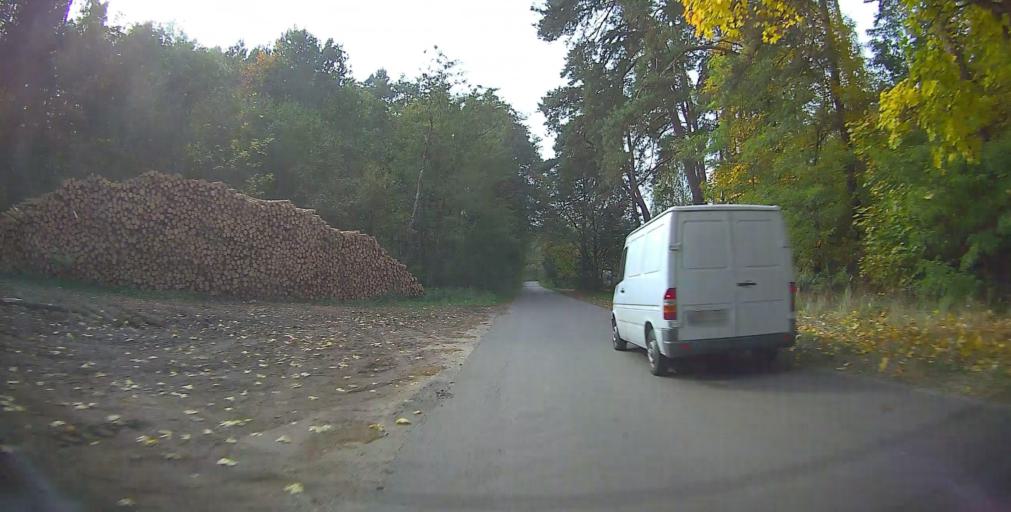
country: PL
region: Masovian Voivodeship
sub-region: Powiat grojecki
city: Mogielnica
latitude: 51.6433
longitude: 20.7531
